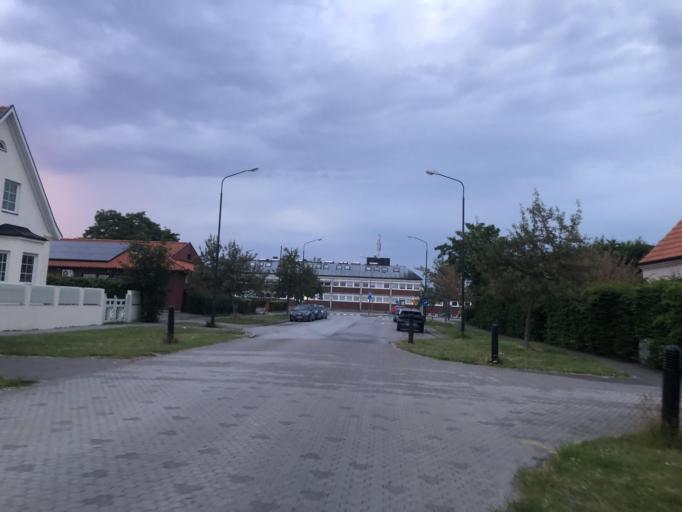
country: SE
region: Skane
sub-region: Burlovs Kommun
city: Arloev
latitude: 55.5982
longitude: 13.0449
